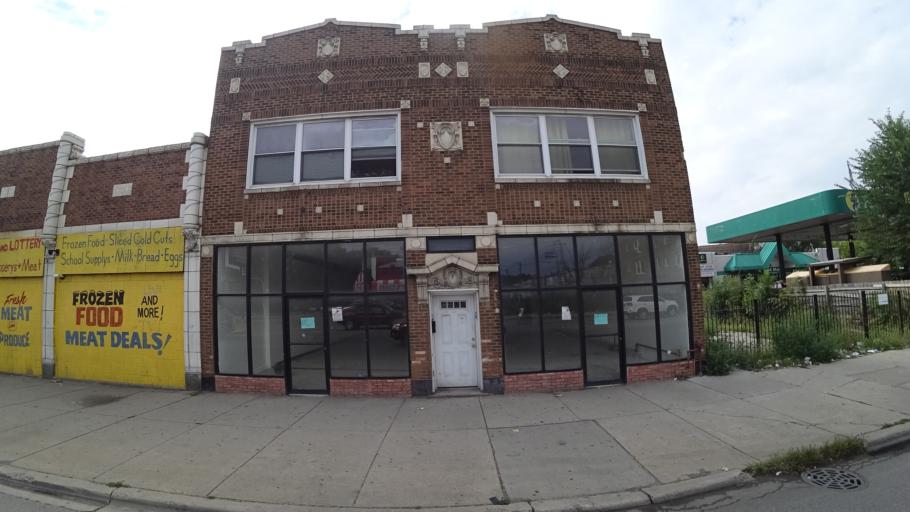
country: US
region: Illinois
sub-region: Cook County
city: Cicero
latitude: 41.8763
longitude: -87.7451
